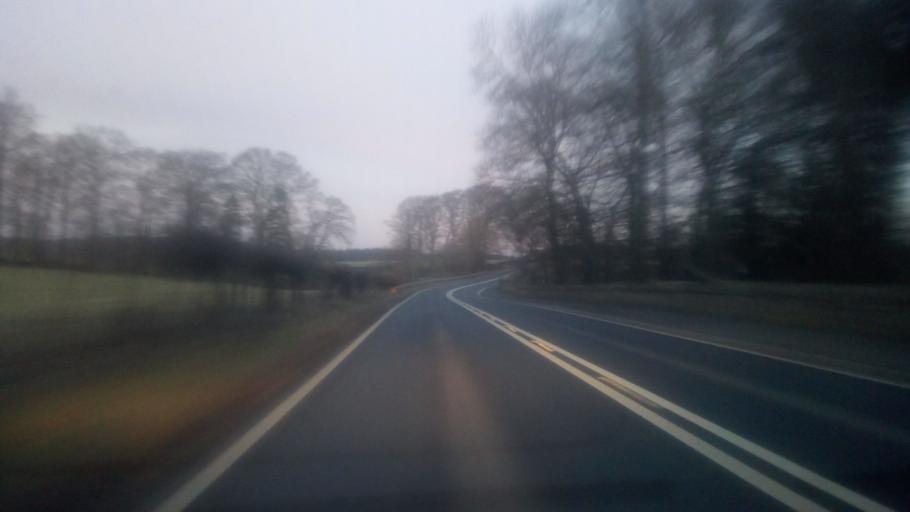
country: GB
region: Scotland
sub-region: The Scottish Borders
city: Lauder
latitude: 55.7260
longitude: -2.7613
